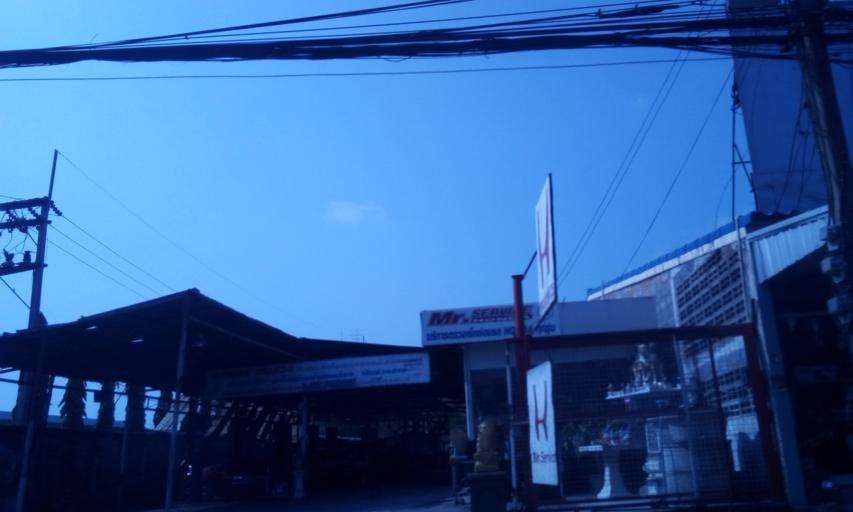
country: TH
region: Bangkok
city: Sai Mai
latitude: 13.9320
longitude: 100.6668
